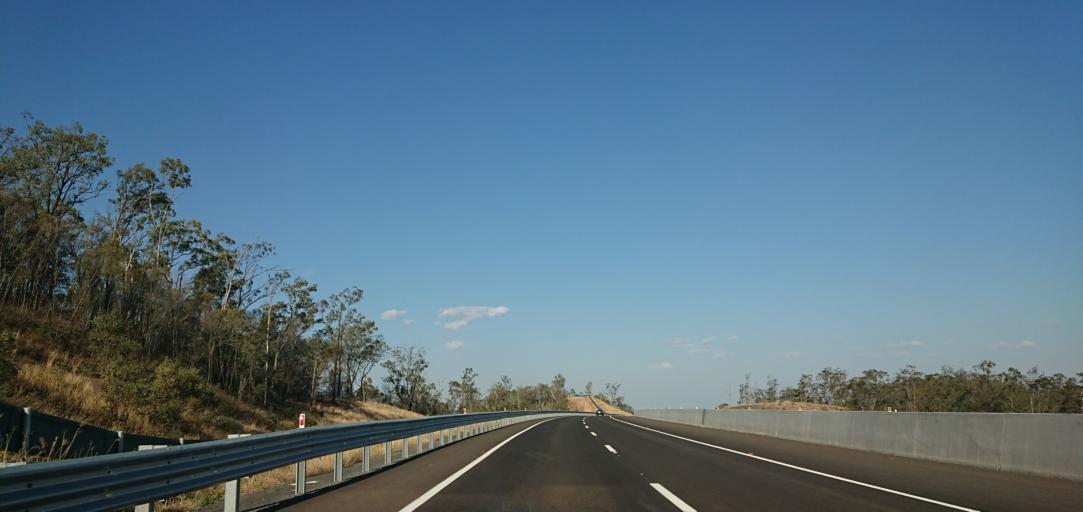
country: AU
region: Queensland
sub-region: Toowoomba
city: East Toowoomba
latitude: -27.5147
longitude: 152.0425
